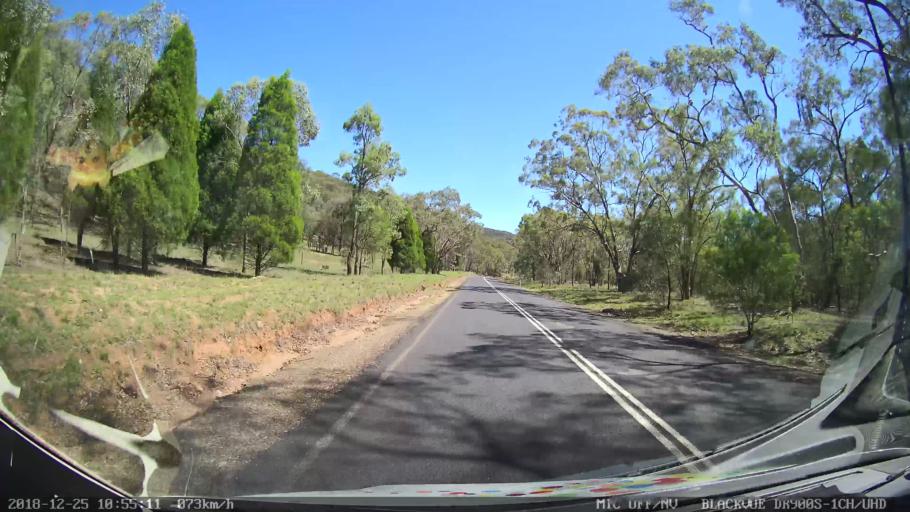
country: AU
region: New South Wales
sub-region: Upper Hunter Shire
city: Merriwa
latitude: -32.4017
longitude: 150.2726
